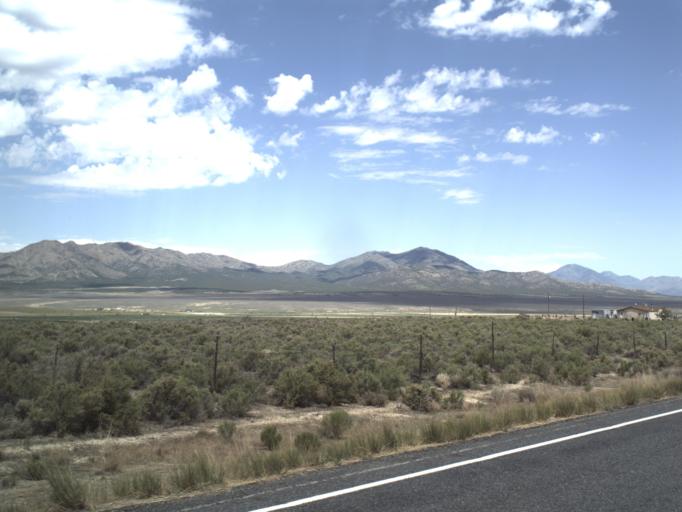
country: US
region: Utah
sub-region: Tooele County
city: Tooele
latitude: 40.1145
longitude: -112.4308
